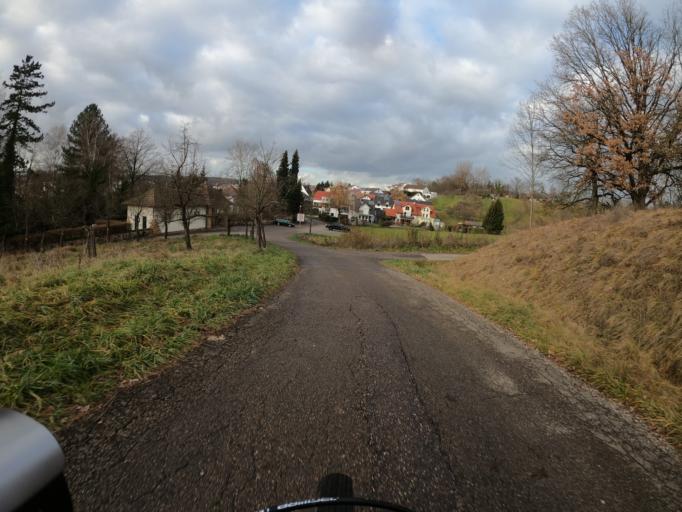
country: DE
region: Baden-Wuerttemberg
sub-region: Regierungsbezirk Stuttgart
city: Wernau
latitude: 48.6862
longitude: 9.4284
